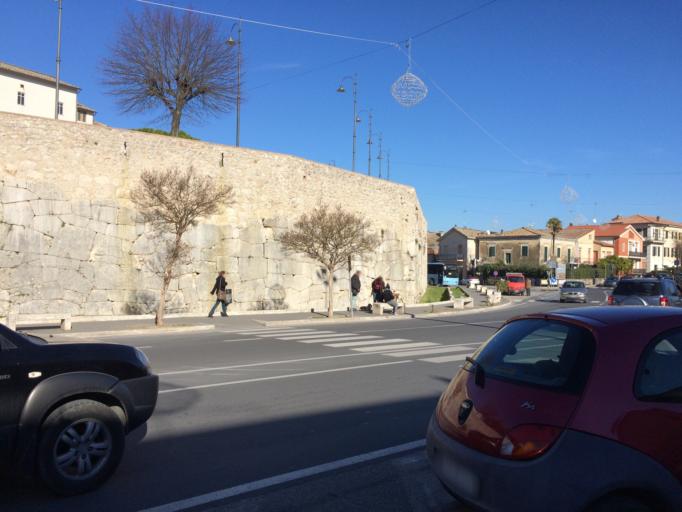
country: IT
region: Umbria
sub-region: Provincia di Terni
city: Amelia
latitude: 42.5535
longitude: 12.4174
